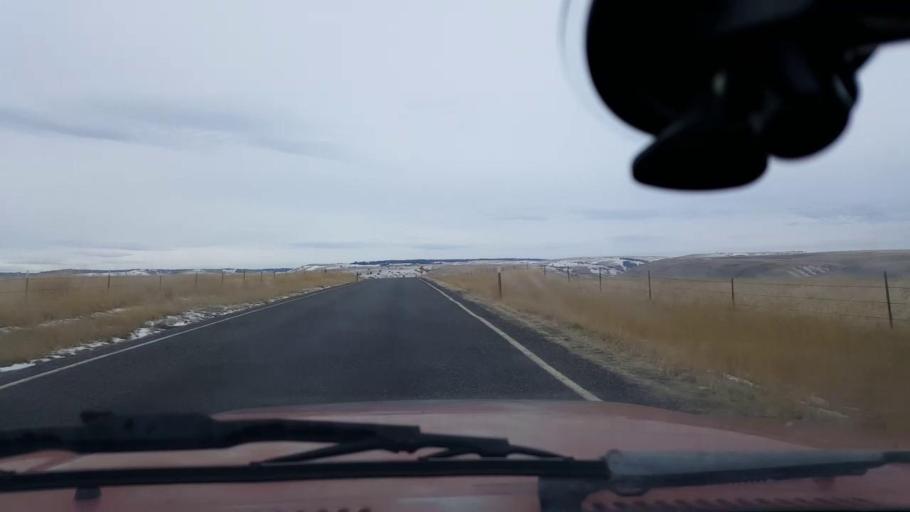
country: US
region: Washington
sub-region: Asotin County
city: Clarkston Heights-Vineland
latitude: 46.3129
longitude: -117.3368
